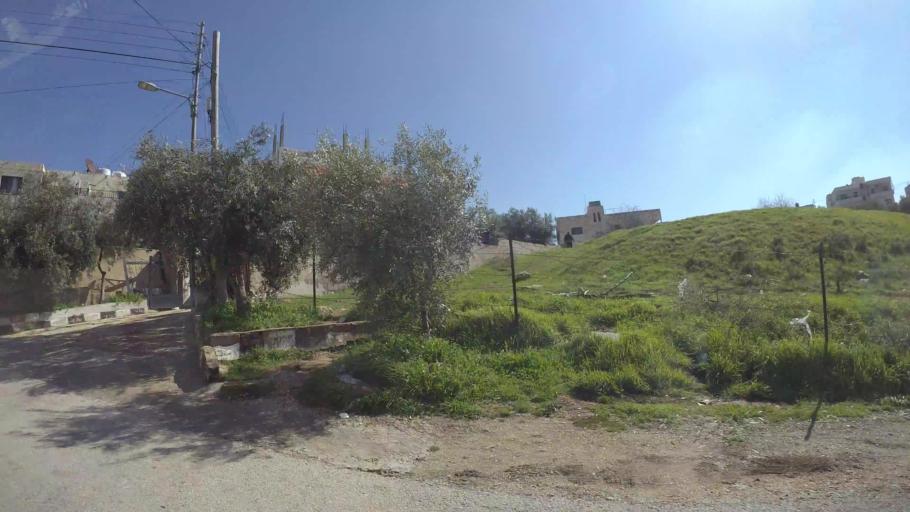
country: JO
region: Amman
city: Al Bunayyat ash Shamaliyah
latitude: 31.9089
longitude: 35.9096
